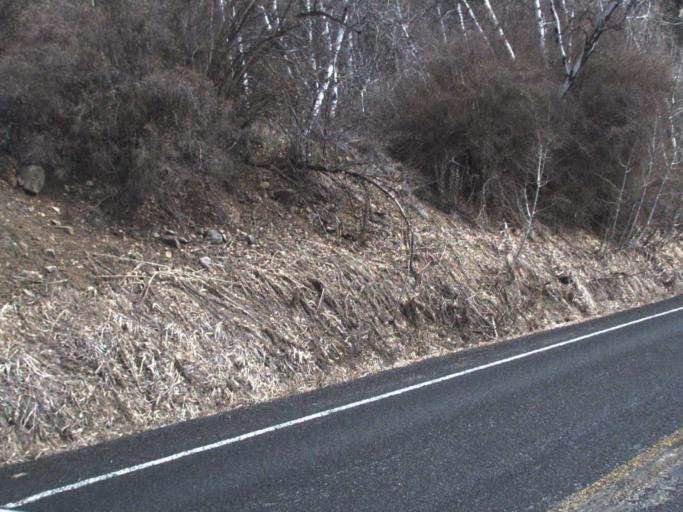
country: US
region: Washington
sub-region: Yakima County
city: Tieton
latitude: 46.8682
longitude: -120.9621
